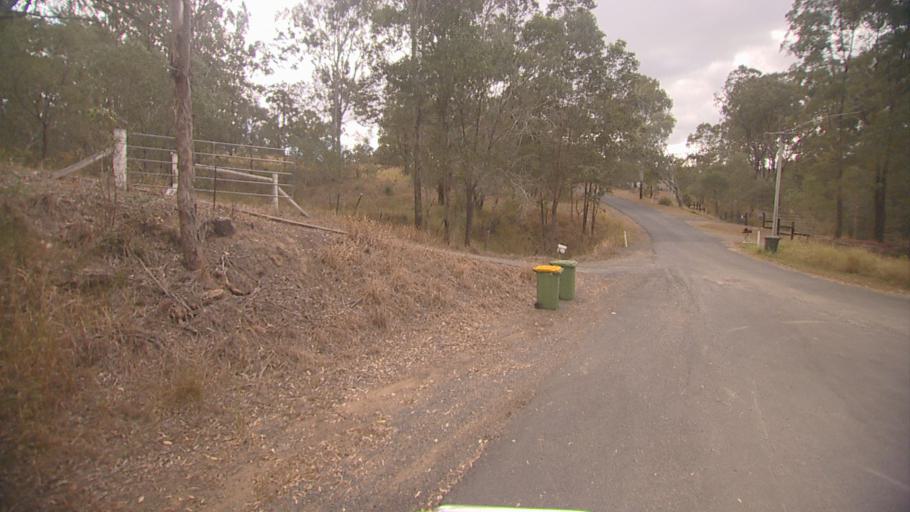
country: AU
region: Queensland
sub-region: Logan
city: Cedar Vale
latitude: -27.8870
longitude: 153.0345
